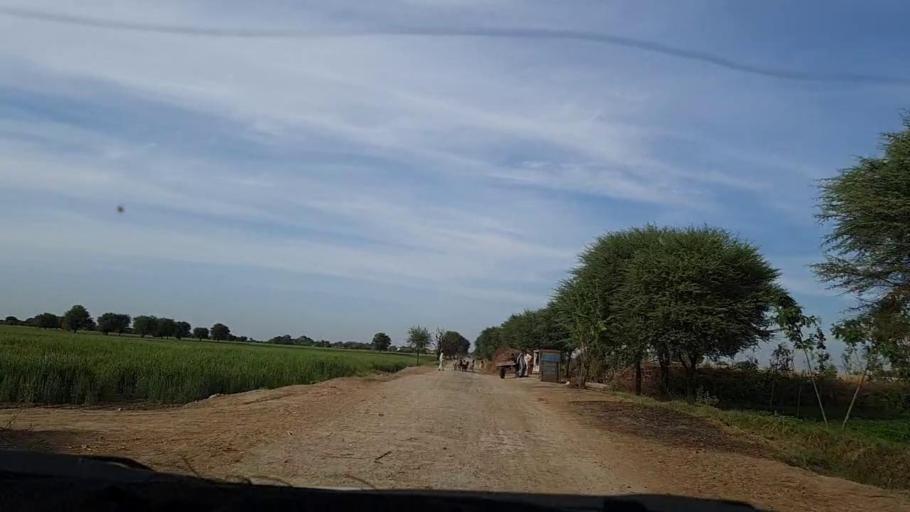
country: PK
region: Sindh
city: Dhoro Naro
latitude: 25.4420
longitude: 69.5123
